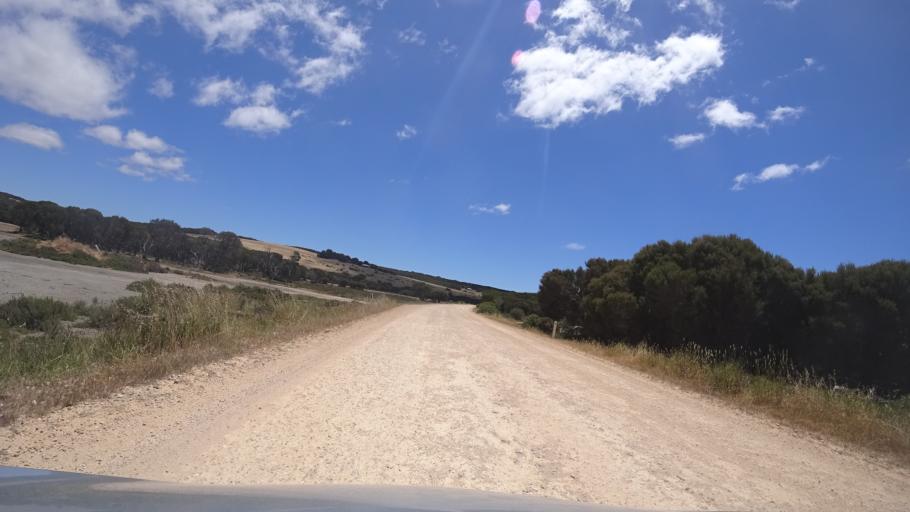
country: AU
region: South Australia
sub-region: Yankalilla
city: Normanville
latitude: -35.8006
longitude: 138.0656
